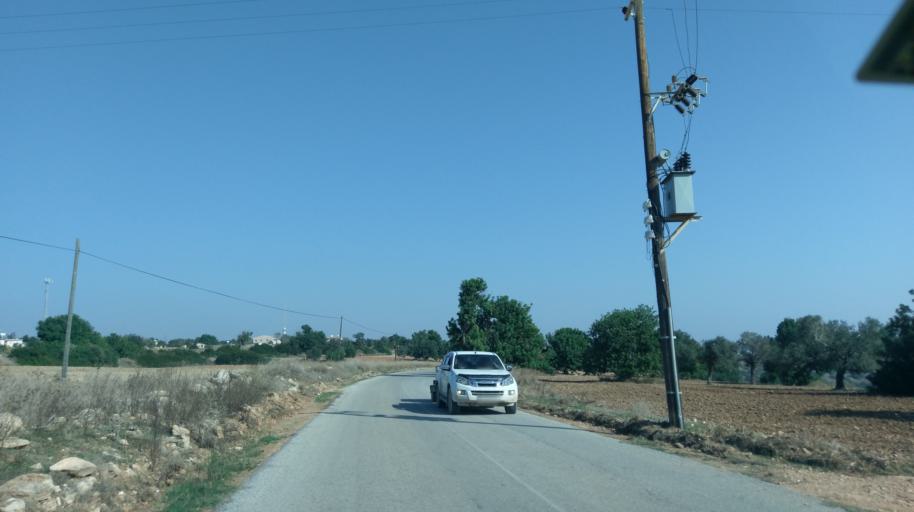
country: CY
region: Ammochostos
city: Leonarisso
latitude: 35.4891
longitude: 34.2083
